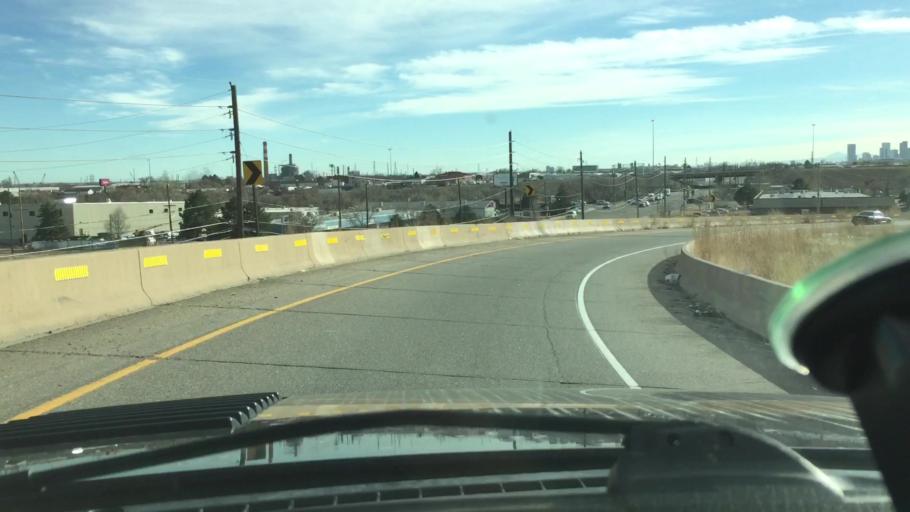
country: US
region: Colorado
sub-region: Adams County
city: Welby
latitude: 39.8267
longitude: -104.9785
